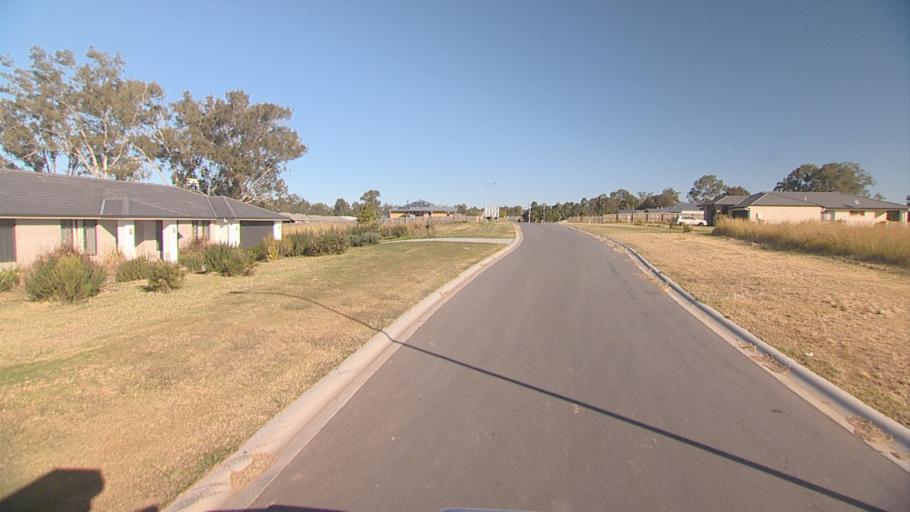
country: AU
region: Queensland
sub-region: Logan
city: North Maclean
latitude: -27.7848
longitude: 153.0257
